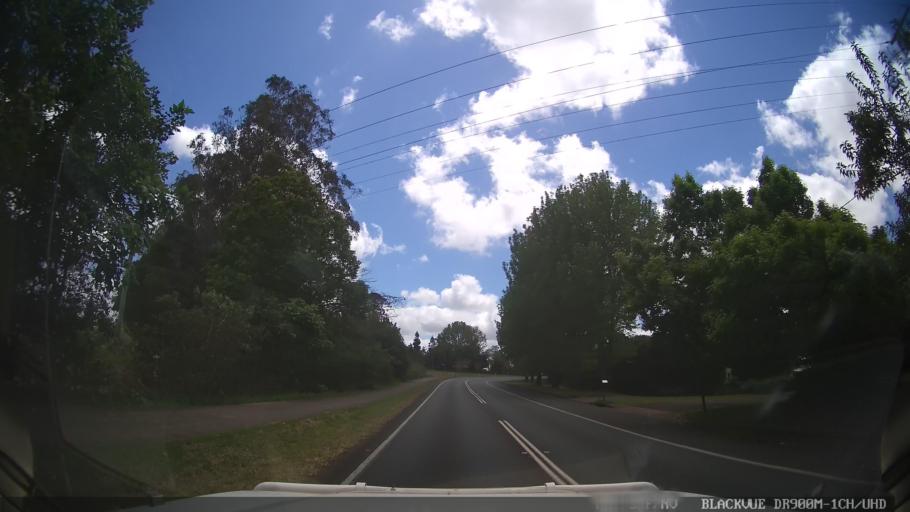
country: AU
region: Queensland
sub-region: Sunshine Coast
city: Nambour
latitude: -26.6653
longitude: 152.8799
